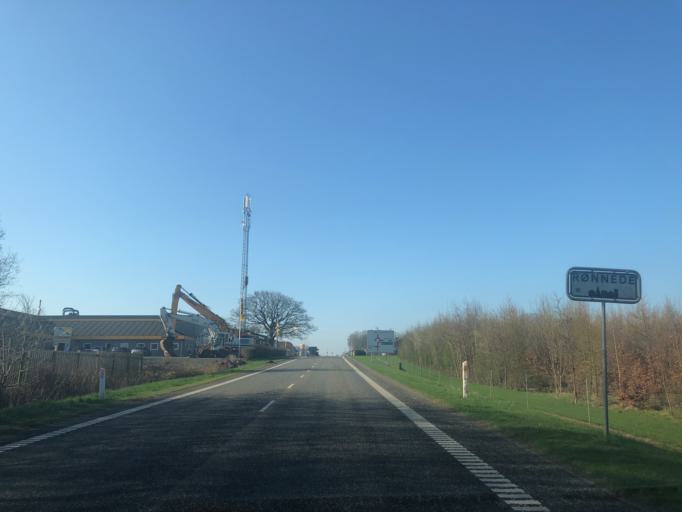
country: DK
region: Zealand
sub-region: Faxe Kommune
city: Ronnede
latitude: 55.2622
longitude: 12.0229
